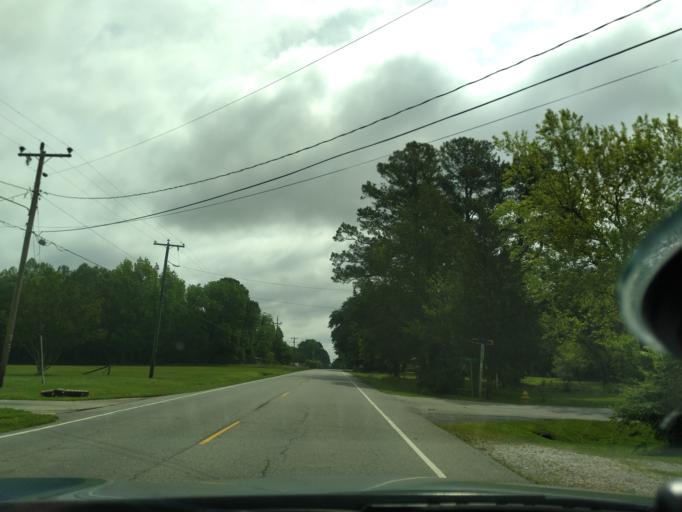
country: US
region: North Carolina
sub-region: Washington County
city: Plymouth
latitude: 35.8739
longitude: -76.6772
